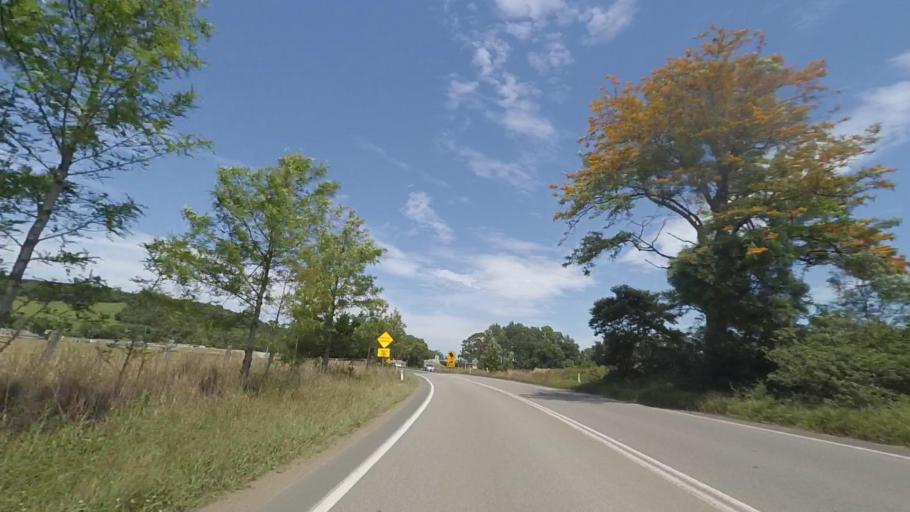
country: AU
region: New South Wales
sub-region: Kiama
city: Gerringong
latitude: -34.7437
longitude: 150.7600
